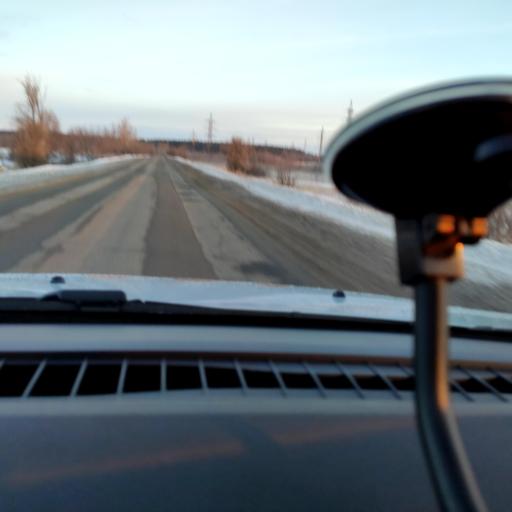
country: RU
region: Samara
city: Samara
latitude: 53.1083
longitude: 50.2260
